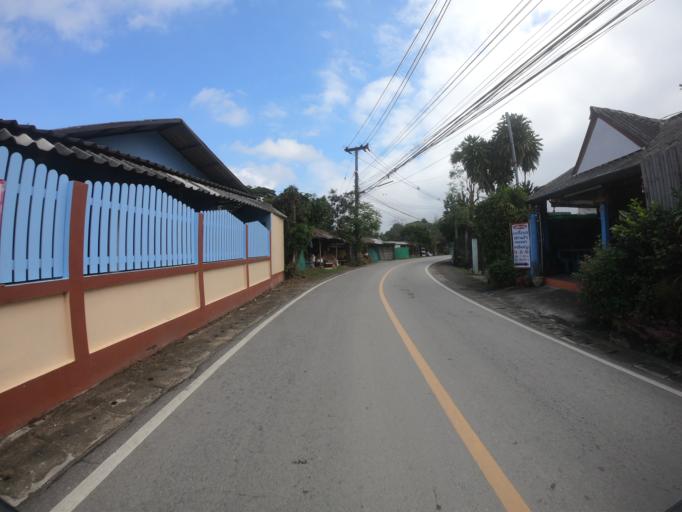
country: TH
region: Chiang Mai
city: Hang Dong
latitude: 18.7261
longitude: 98.9532
